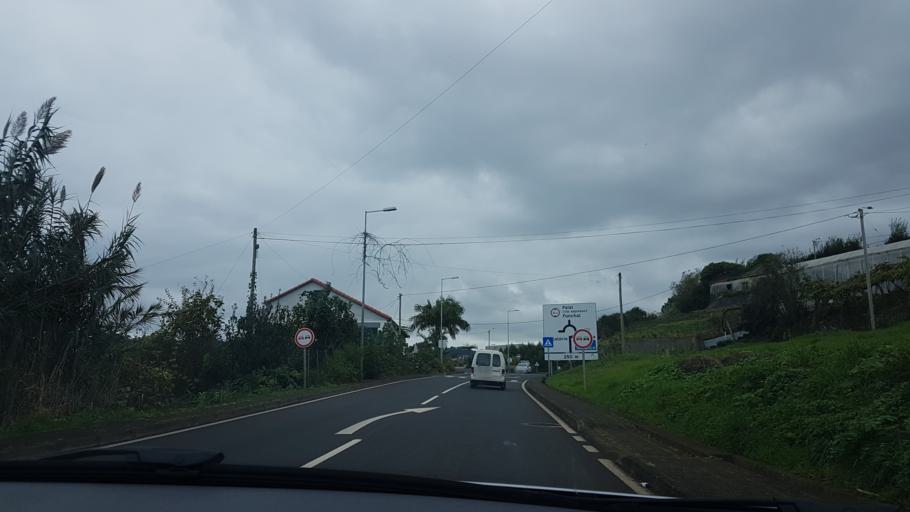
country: PT
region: Madeira
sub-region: Santana
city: Santana
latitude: 32.8131
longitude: -16.8862
